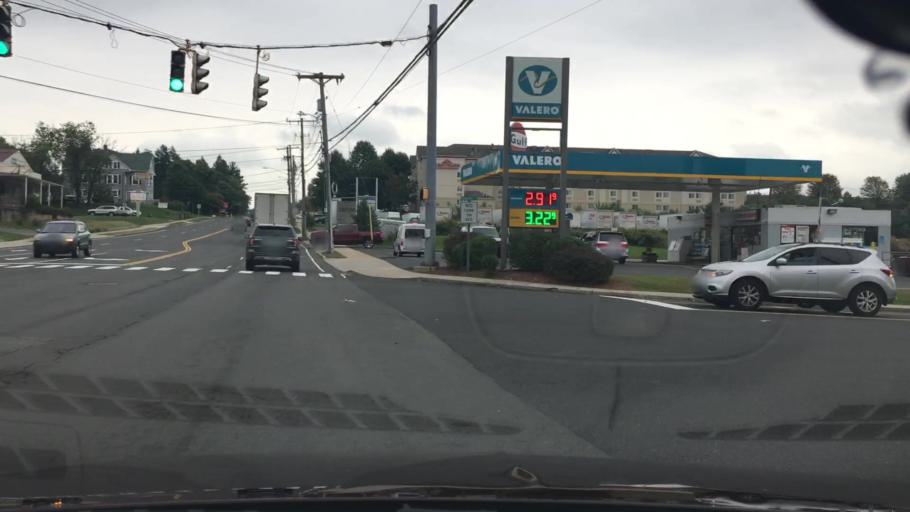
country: US
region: Connecticut
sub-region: New Haven County
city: Meriden
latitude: 41.5260
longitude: -72.7674
